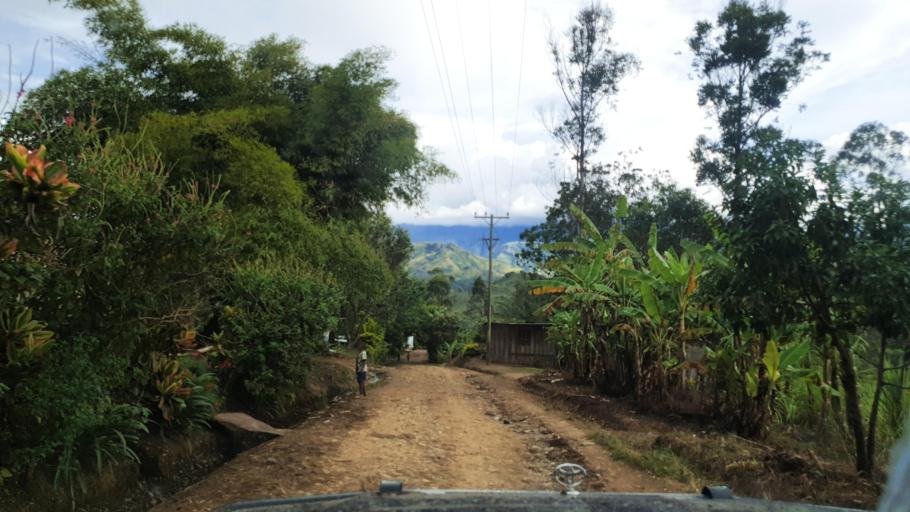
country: PG
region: Jiwaka
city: Minj
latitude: -5.9346
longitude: 144.8085
